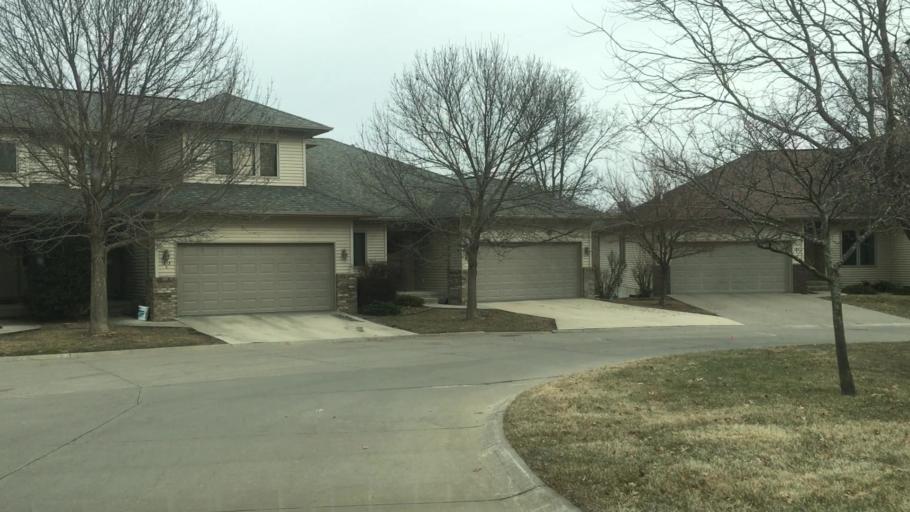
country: US
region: Iowa
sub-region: Johnson County
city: Coralville
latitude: 41.7001
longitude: -91.5858
